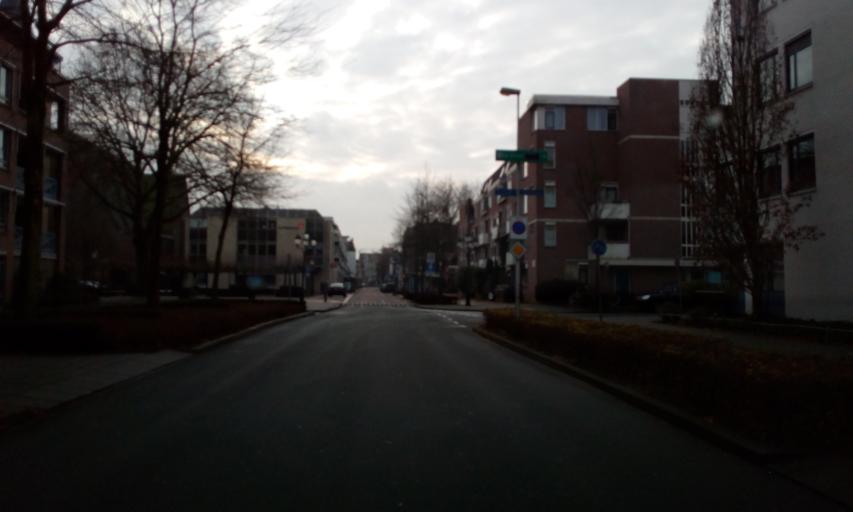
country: NL
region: North Holland
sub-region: Gemeente Bussum
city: Bussum
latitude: 52.2769
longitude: 5.1626
